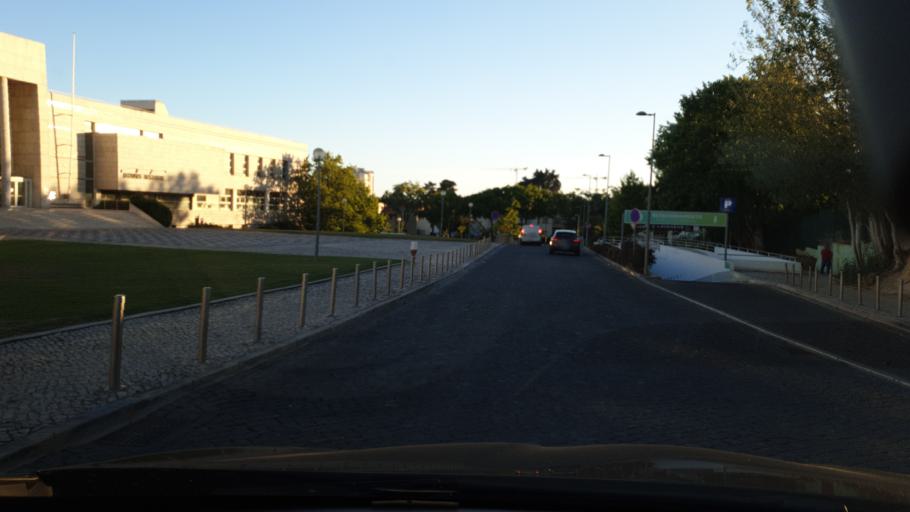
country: PT
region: Lisbon
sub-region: Cascais
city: Cascais
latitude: 38.7019
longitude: -9.4275
